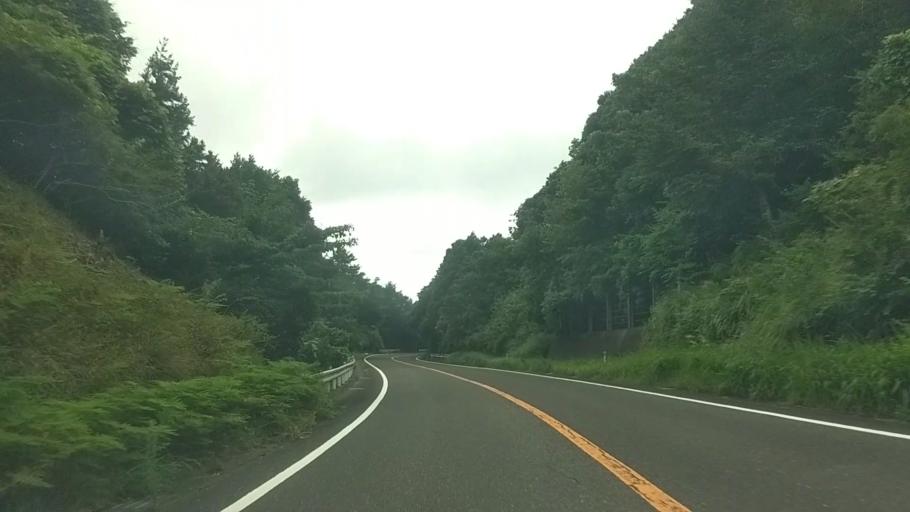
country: JP
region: Chiba
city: Kawaguchi
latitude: 35.2153
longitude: 140.0483
